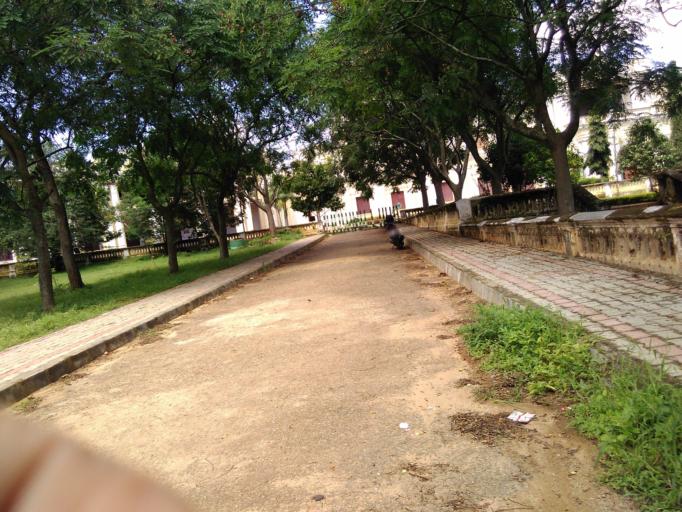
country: IN
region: Karnataka
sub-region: Mysore
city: Mysore
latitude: 12.3136
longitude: 76.6233
